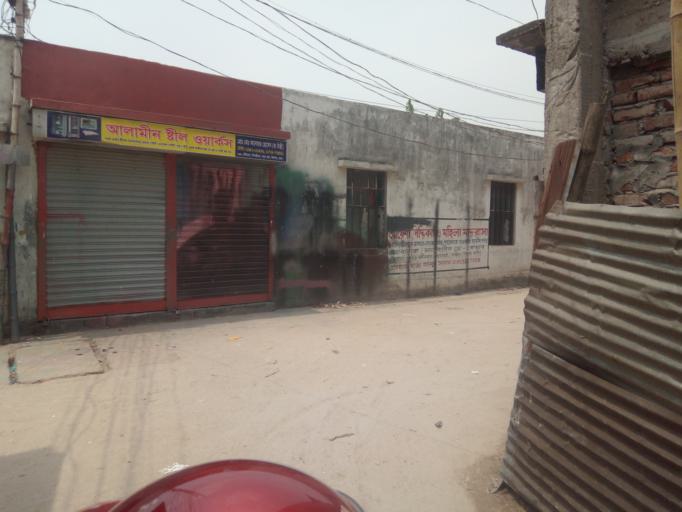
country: BD
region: Dhaka
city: Paltan
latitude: 23.7565
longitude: 90.4277
